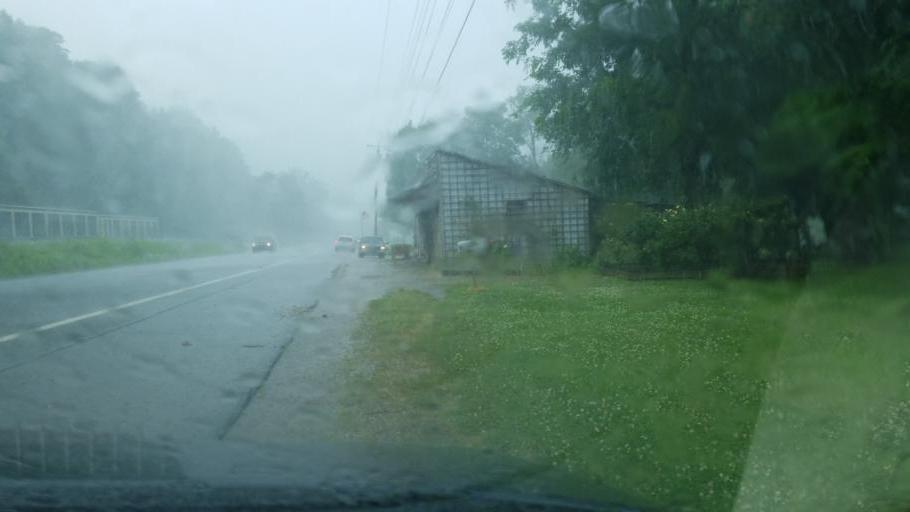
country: US
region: Tennessee
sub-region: Humphreys County
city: McEwen
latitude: 36.1037
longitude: -87.7082
